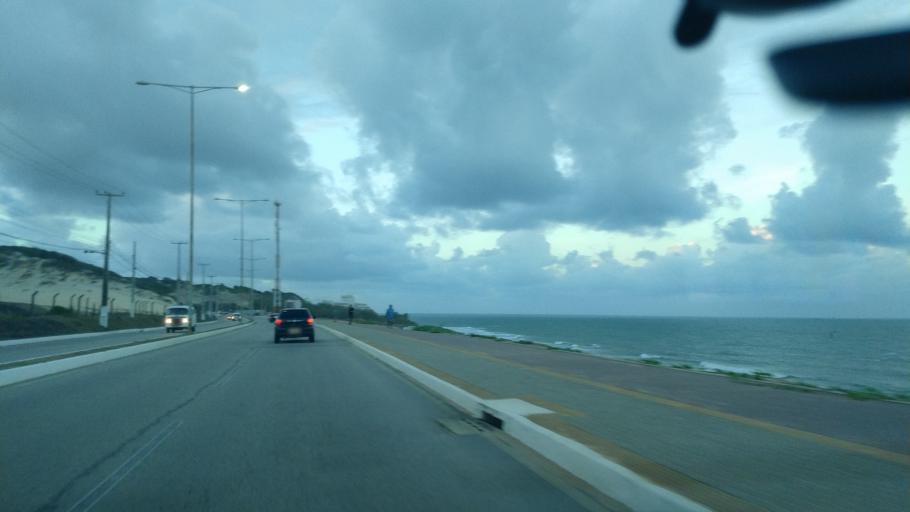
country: BR
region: Rio Grande do Norte
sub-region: Natal
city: Natal
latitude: -5.8482
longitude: -35.1822
